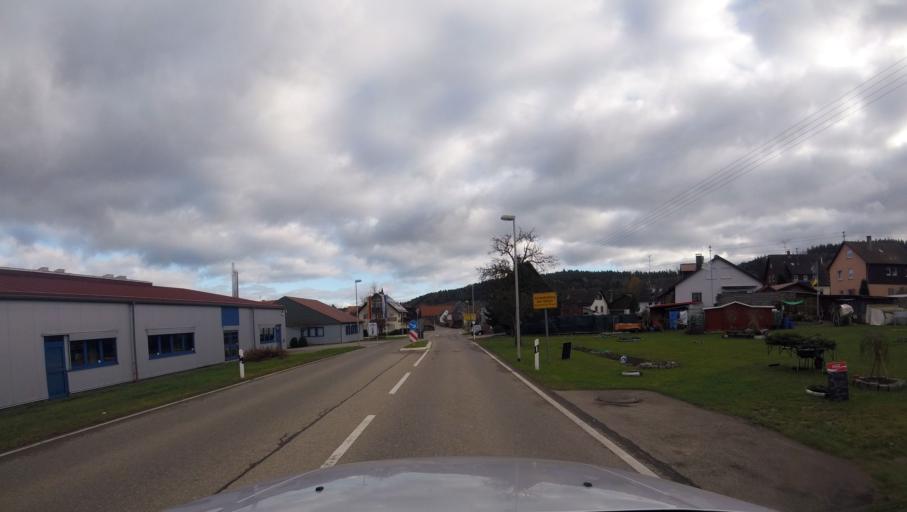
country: DE
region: Baden-Wuerttemberg
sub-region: Regierungsbezirk Stuttgart
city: Kaisersbach
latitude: 48.9509
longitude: 9.6798
